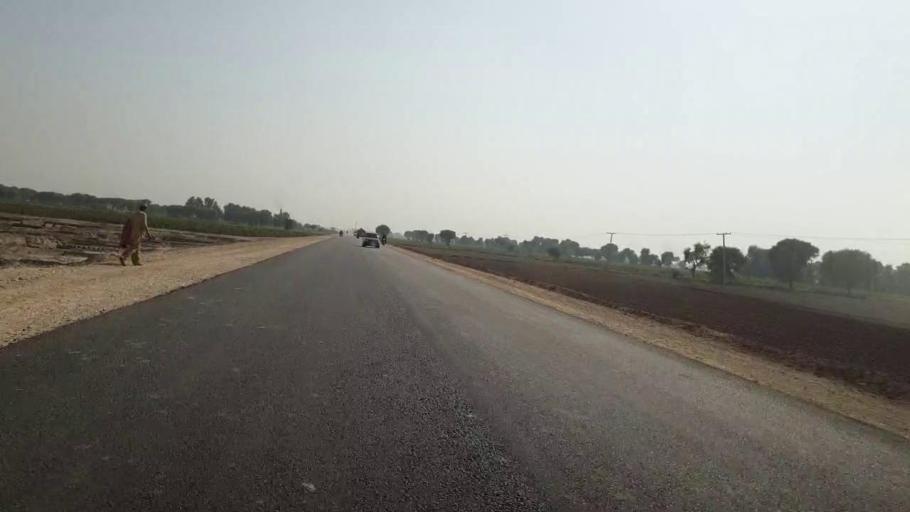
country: PK
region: Sindh
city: Dadu
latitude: 26.6656
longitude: 67.7765
